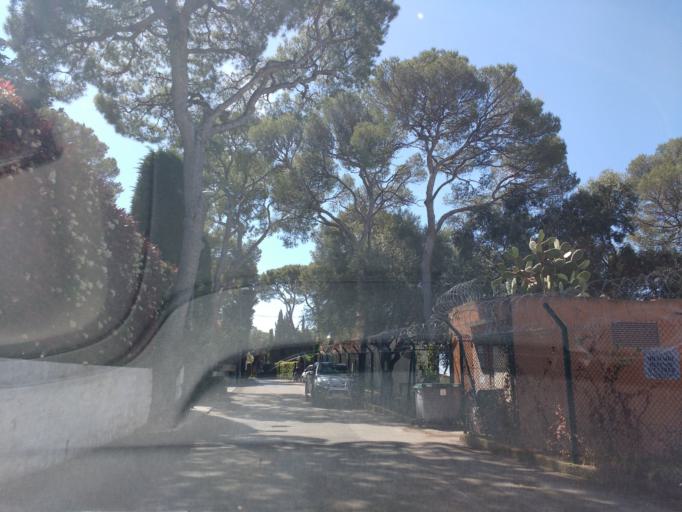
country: FR
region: Provence-Alpes-Cote d'Azur
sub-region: Departement des Alpes-Maritimes
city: Saint-Jean-Cap-Ferrat
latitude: 43.6777
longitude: 7.3261
